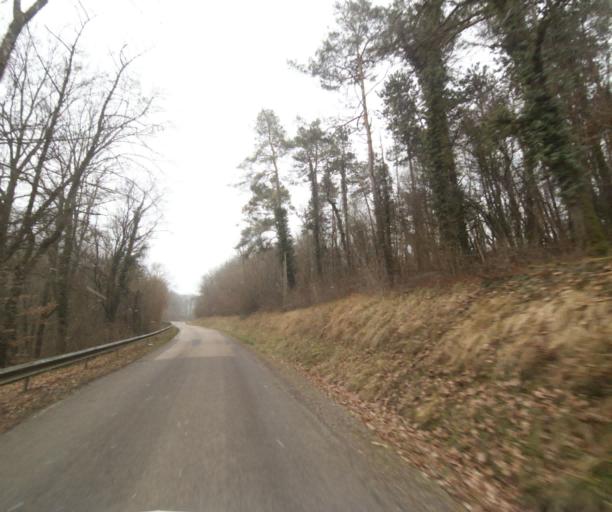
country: FR
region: Champagne-Ardenne
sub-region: Departement de la Haute-Marne
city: Chevillon
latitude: 48.5199
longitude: 5.0915
